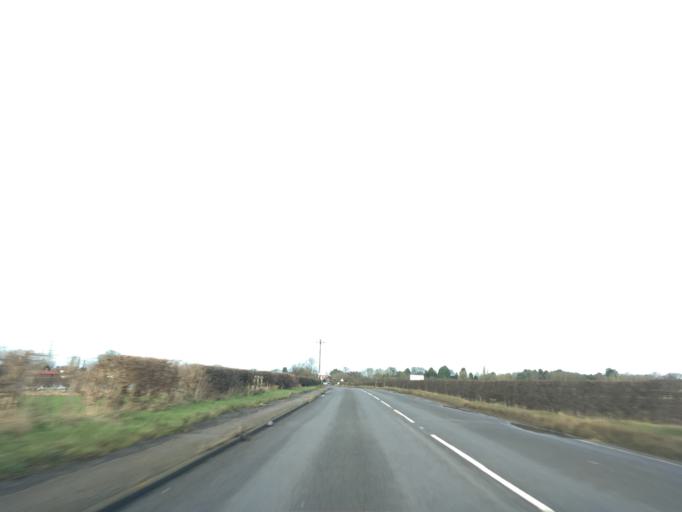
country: GB
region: England
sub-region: Nottinghamshire
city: South Collingham
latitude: 53.1689
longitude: -0.7648
